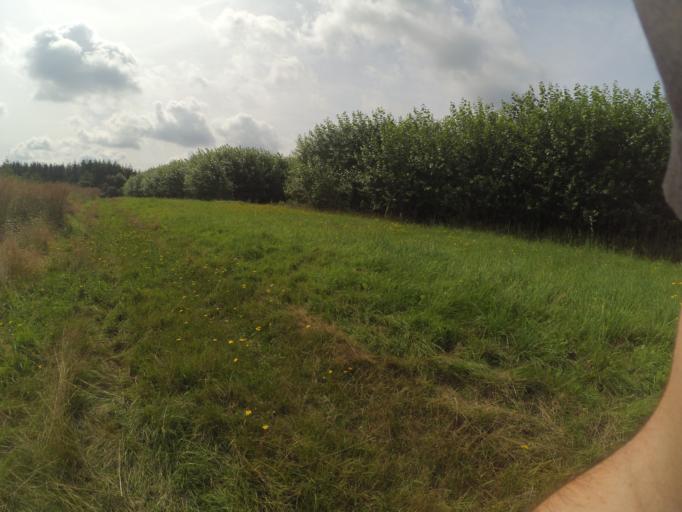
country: DE
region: Hesse
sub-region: Regierungsbezirk Kassel
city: Kirchheim
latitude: 50.8603
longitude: 9.5338
